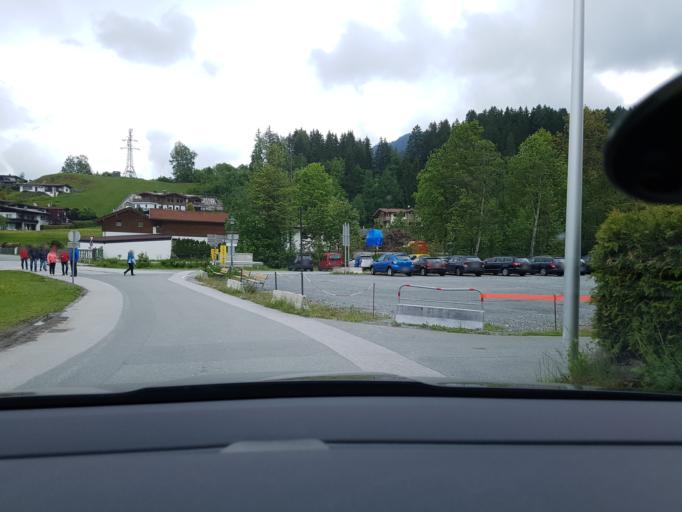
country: AT
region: Tyrol
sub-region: Politischer Bezirk Kufstein
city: Ellmau
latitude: 47.5105
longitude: 12.2928
